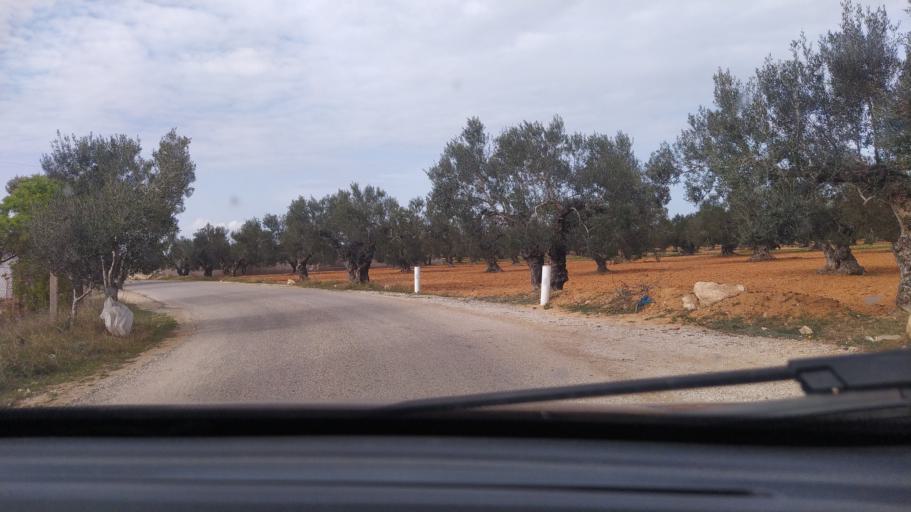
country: TN
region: Al Munastir
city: Sidi Bin Nur
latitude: 35.5233
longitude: 10.9701
